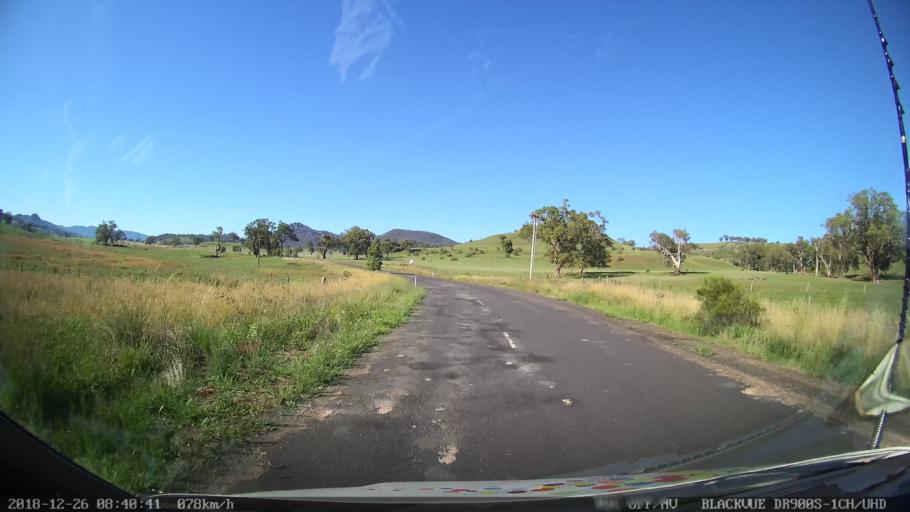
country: AU
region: New South Wales
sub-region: Mid-Western Regional
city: Kandos
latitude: -32.4695
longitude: 150.0747
